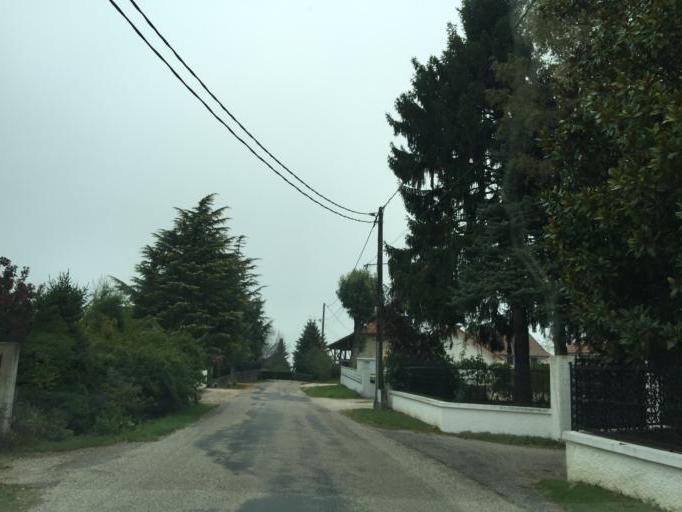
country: FR
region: Rhone-Alpes
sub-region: Departement de l'Isere
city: Faverges-de-la-Tour
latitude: 45.5917
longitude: 5.5154
